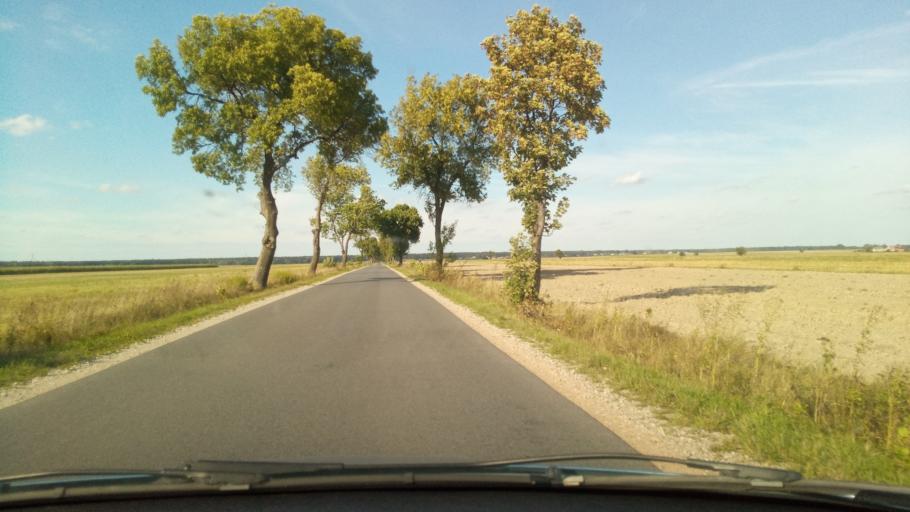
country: PL
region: Lodz Voivodeship
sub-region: Powiat piotrkowski
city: Sulejow
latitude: 51.3837
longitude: 19.8186
